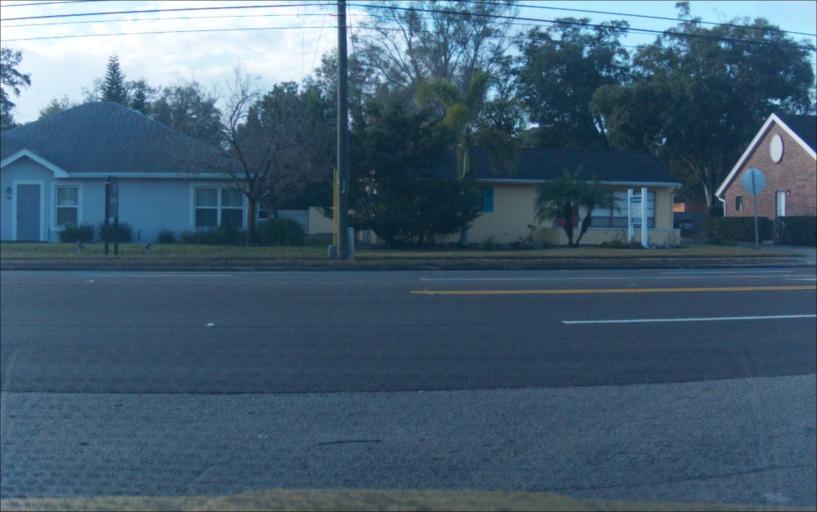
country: US
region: Florida
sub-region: Orange County
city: Maitland
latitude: 28.6269
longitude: -81.3449
